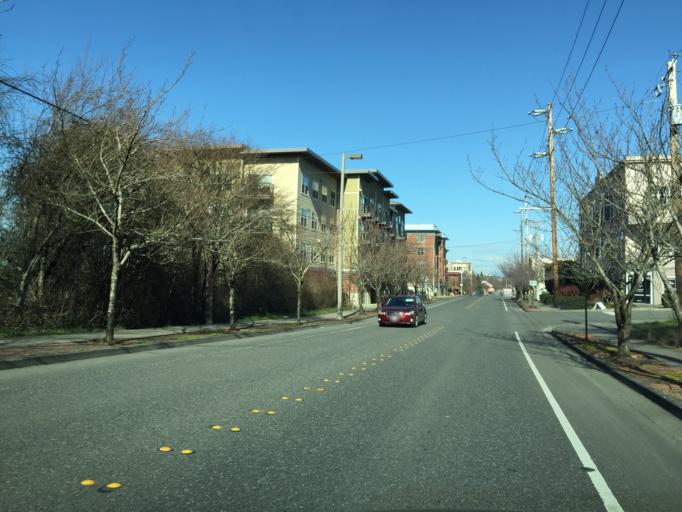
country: US
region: Washington
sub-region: Whatcom County
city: Bellingham
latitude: 48.7183
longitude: -122.5045
